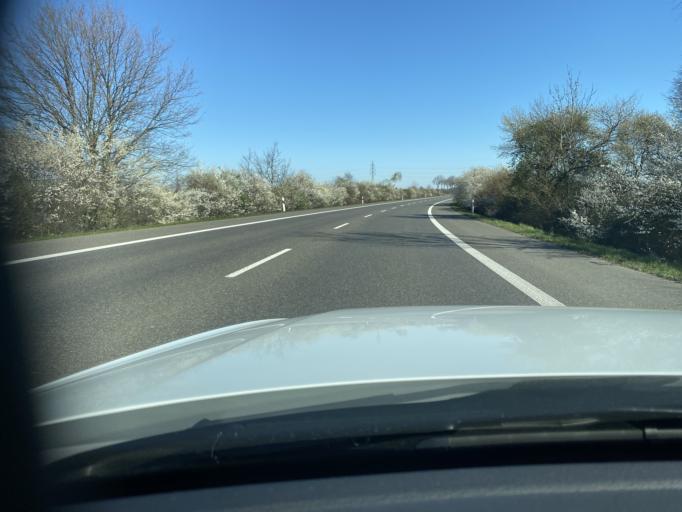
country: DE
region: North Rhine-Westphalia
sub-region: Regierungsbezirk Dusseldorf
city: Grevenbroich
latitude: 51.0880
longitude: 6.6104
